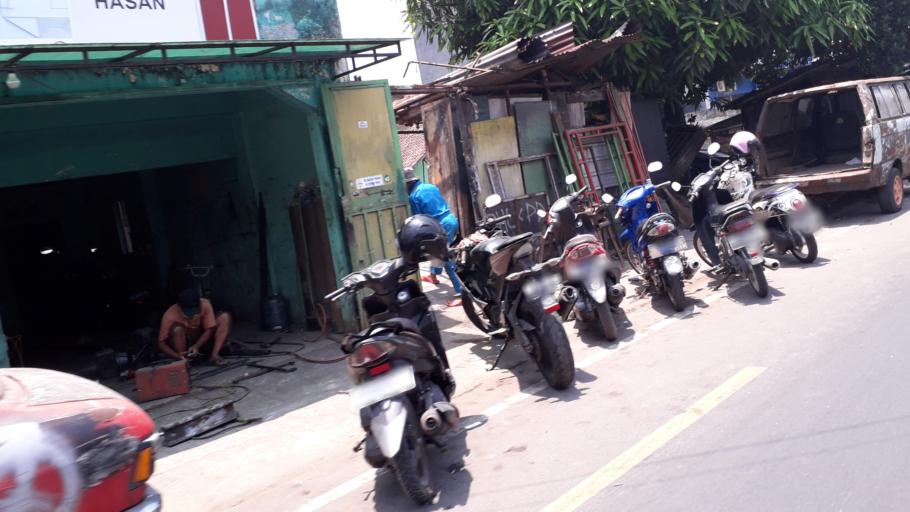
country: ID
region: Daerah Istimewa Yogyakarta
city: Yogyakarta
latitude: -7.7626
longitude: 110.3694
